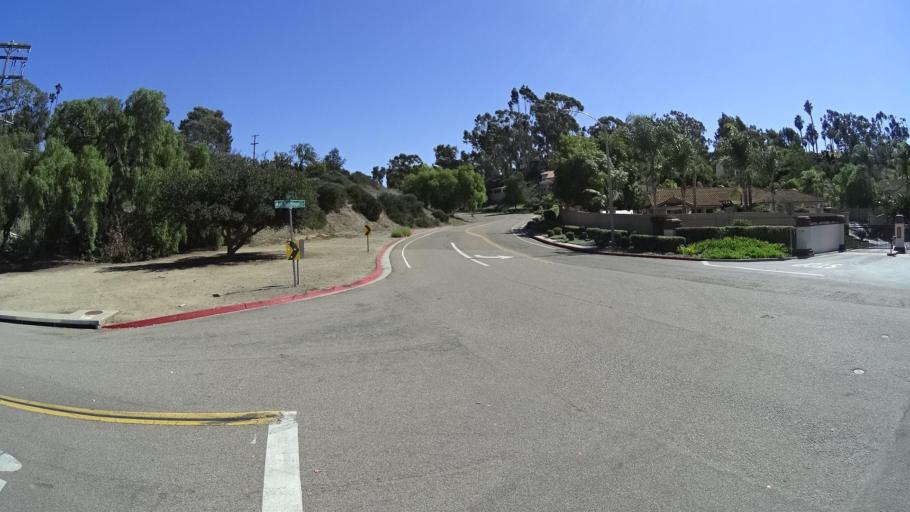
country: US
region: California
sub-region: San Diego County
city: Bonita
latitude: 32.6644
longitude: -117.0516
